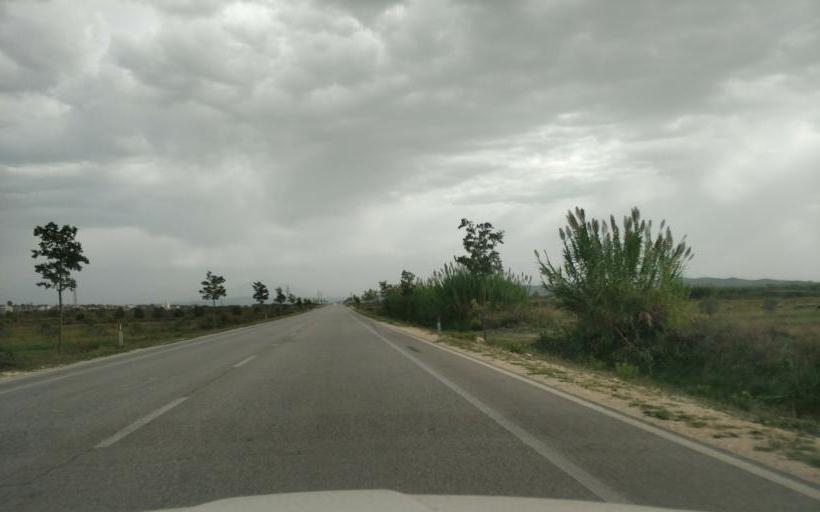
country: AL
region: Fier
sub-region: Rrethi i Fierit
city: Frakulla e Madhe
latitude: 40.6472
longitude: 19.4971
